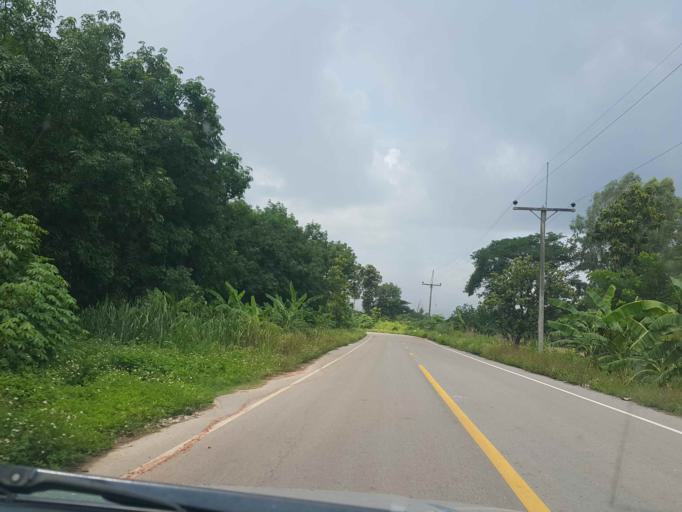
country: TH
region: Phayao
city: Dok Kham Tai
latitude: 19.0483
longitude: 99.9509
